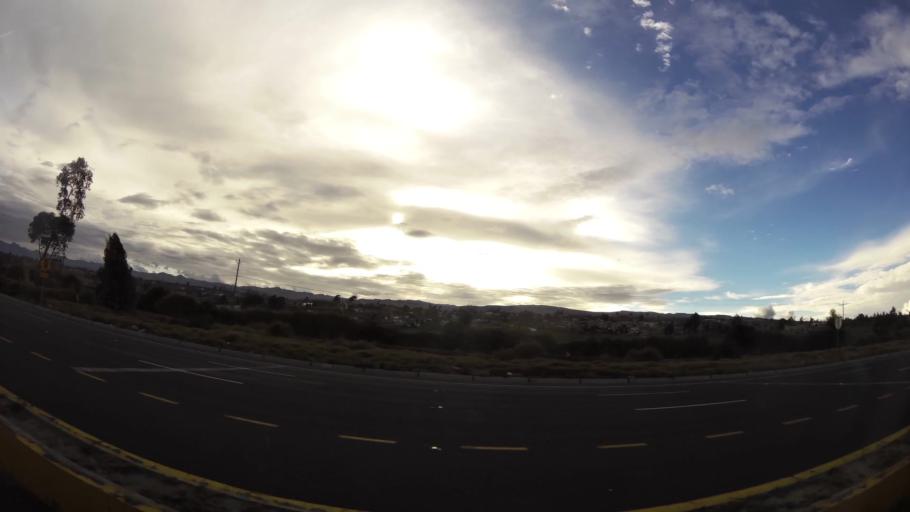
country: EC
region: Cotopaxi
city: Latacunga
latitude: -0.9052
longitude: -78.6285
